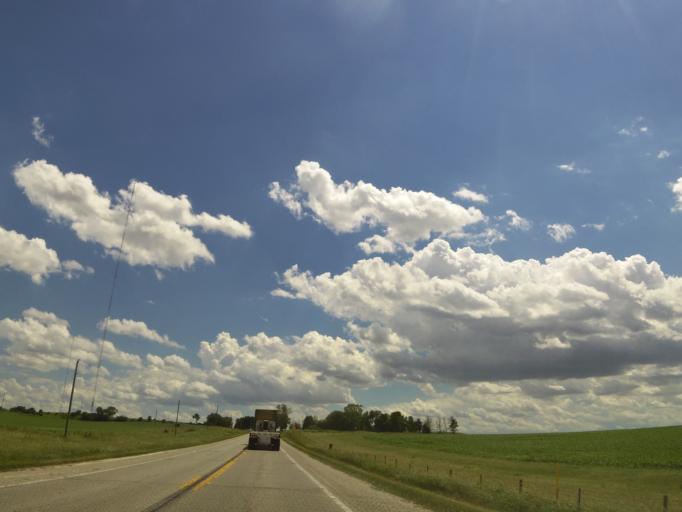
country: US
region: Iowa
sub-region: Benton County
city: Urbana
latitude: 42.3025
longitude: -91.8897
